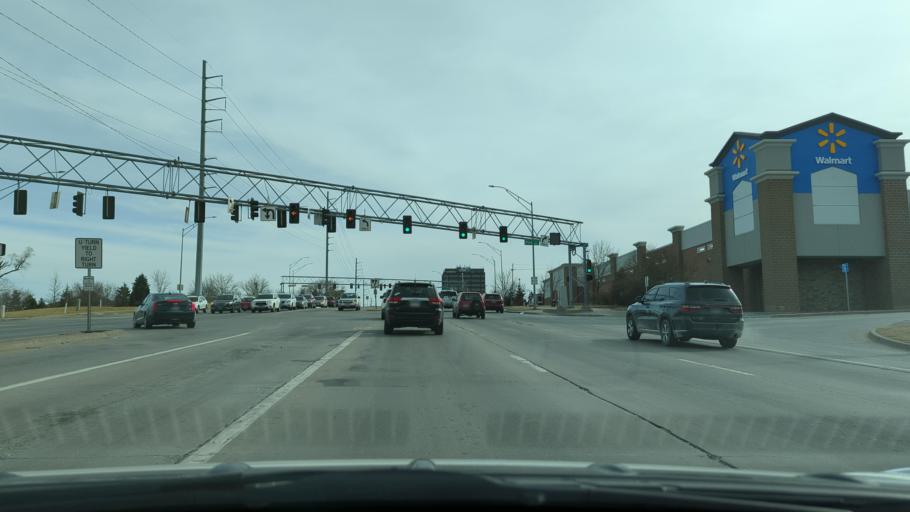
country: US
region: Nebraska
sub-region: Douglas County
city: Ralston
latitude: 41.2450
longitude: -96.0241
